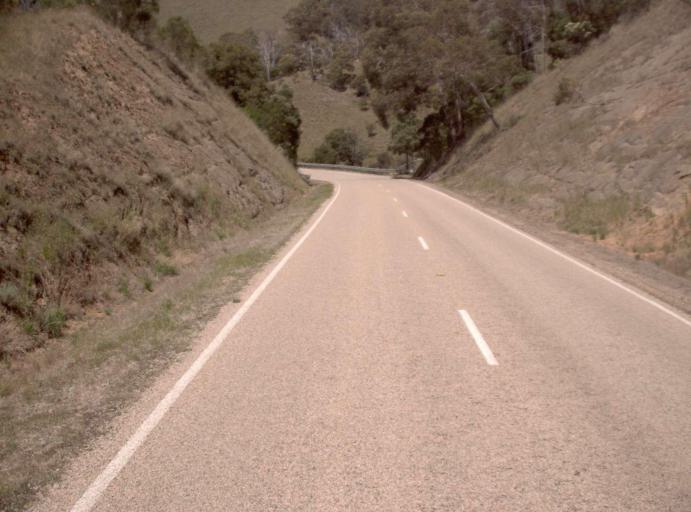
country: AU
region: Victoria
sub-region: Alpine
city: Mount Beauty
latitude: -37.1634
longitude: 147.6579
